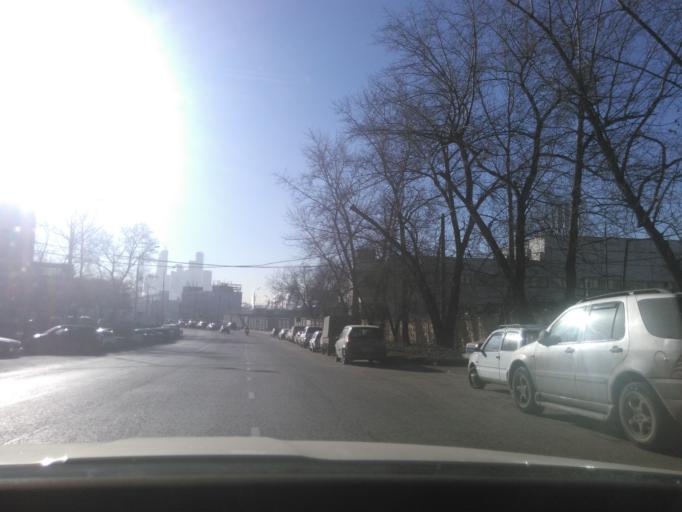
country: RU
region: Moskovskaya
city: Khoroshevo-Mnevniki
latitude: 55.7731
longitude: 37.4981
